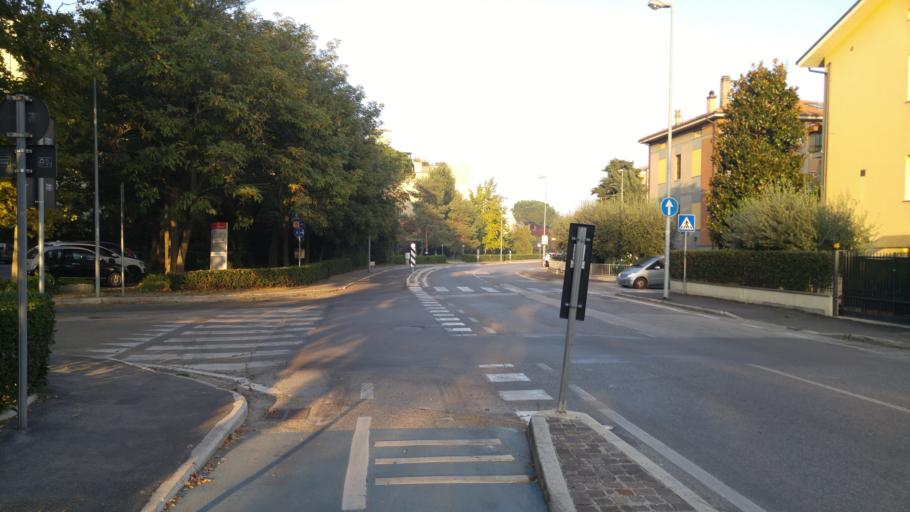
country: IT
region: The Marches
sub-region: Provincia di Pesaro e Urbino
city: Pesaro
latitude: 43.8973
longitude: 12.8881
